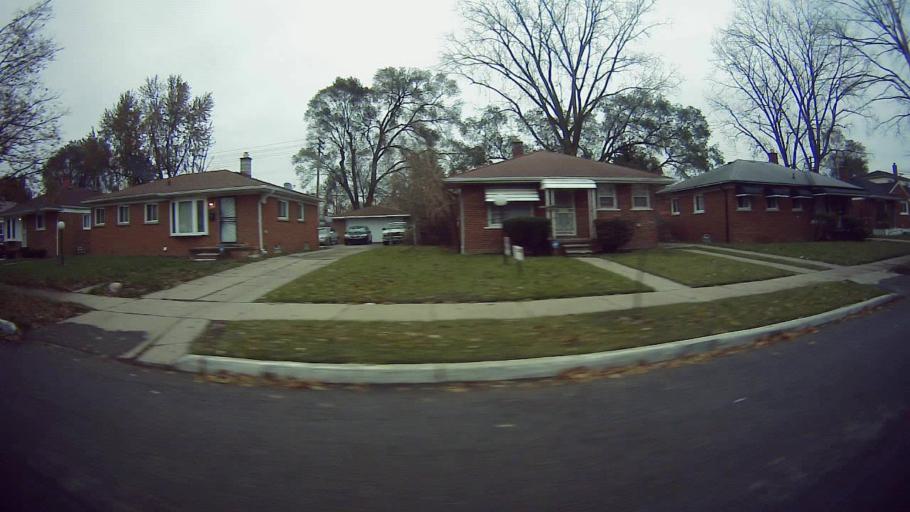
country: US
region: Michigan
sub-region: Wayne County
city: Highland Park
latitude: 42.4266
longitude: -83.0826
